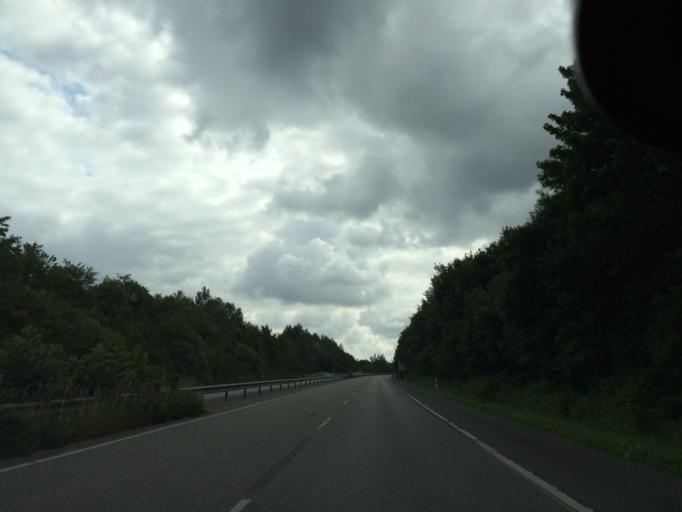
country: DE
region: Schleswig-Holstein
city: Kronshagen
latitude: 54.3516
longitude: 10.1101
